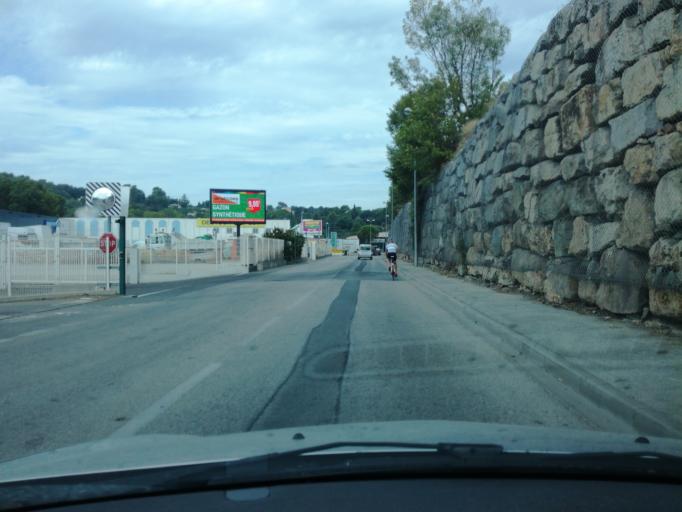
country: FR
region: Provence-Alpes-Cote d'Azur
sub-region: Departement du Var
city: Draguignan
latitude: 43.5275
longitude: 6.4513
